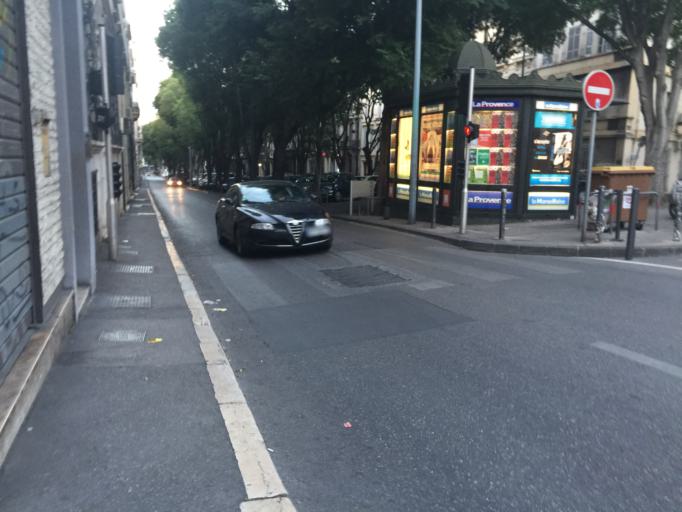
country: FR
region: Provence-Alpes-Cote d'Azur
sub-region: Departement des Bouches-du-Rhone
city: Marseille 02
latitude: 43.2901
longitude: 5.3724
